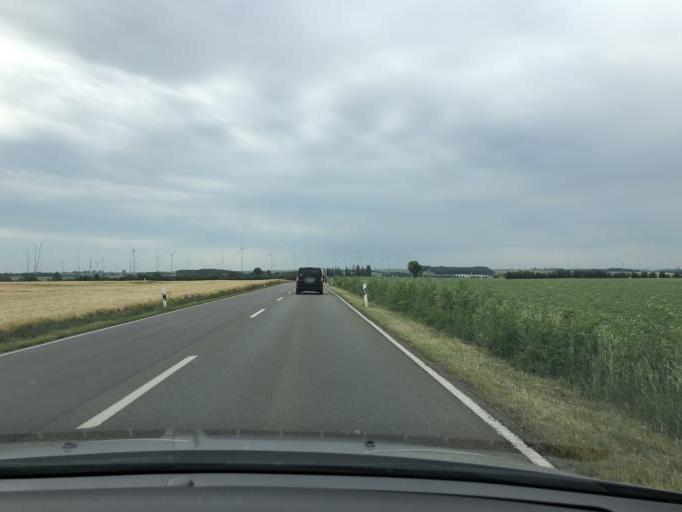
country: DE
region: Saxony-Anhalt
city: Prittitz
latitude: 51.1687
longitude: 11.9294
